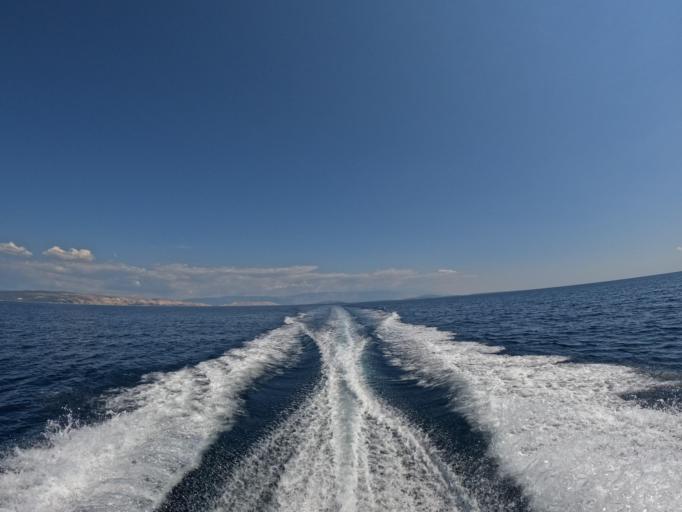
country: HR
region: Primorsko-Goranska
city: Cres
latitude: 44.9347
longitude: 14.5124
